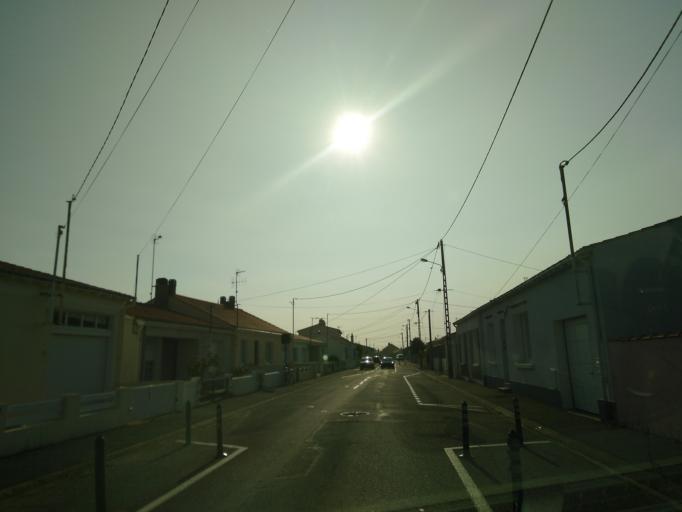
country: FR
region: Pays de la Loire
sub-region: Departement de la Vendee
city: Les Sables-d'Olonne
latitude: 46.4967
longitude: -1.8042
